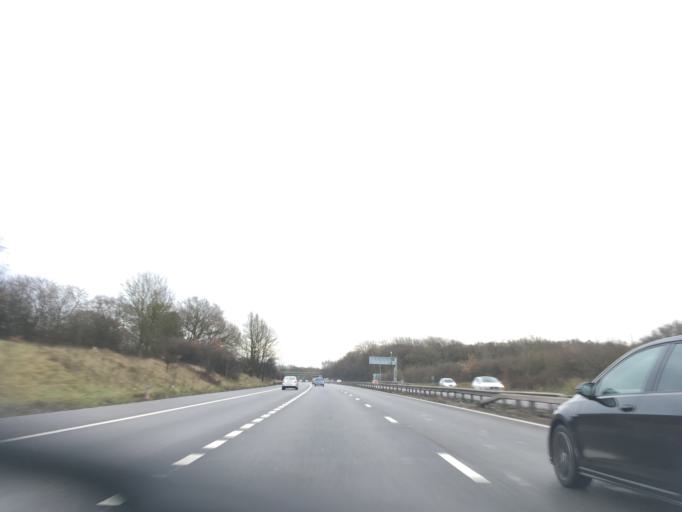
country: GB
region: England
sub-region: Solihull
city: Dickens Heath
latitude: 52.3485
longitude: -1.8339
